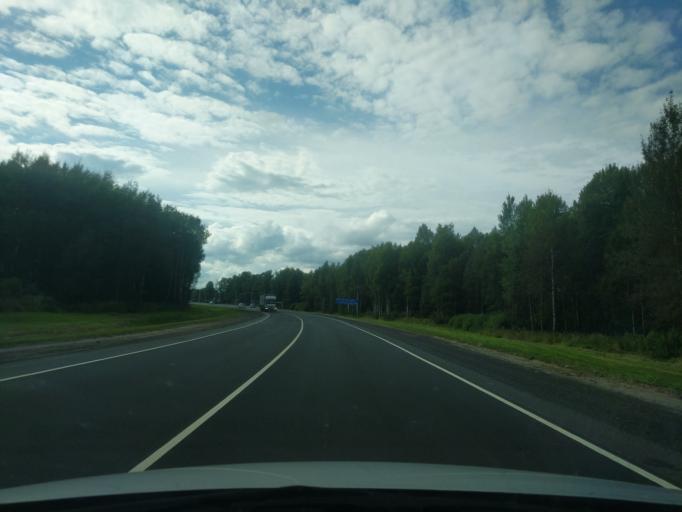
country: RU
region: Jaroslavl
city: Nekrasovskoye
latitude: 57.6370
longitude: 40.3962
